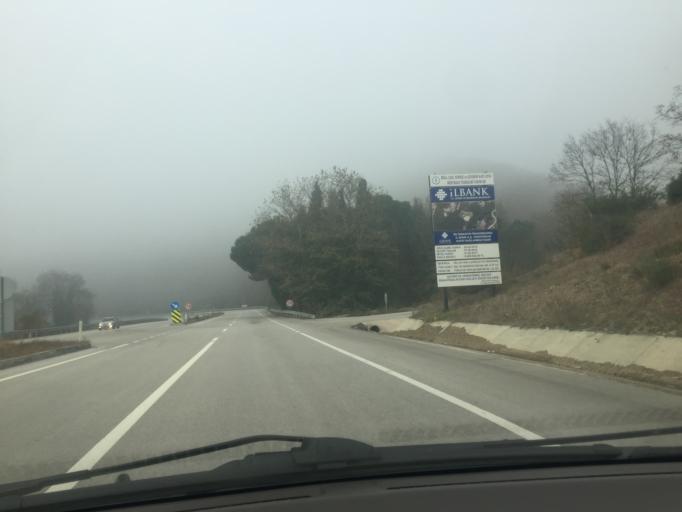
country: TR
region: Canakkale
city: Biga
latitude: 40.1273
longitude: 27.1922
